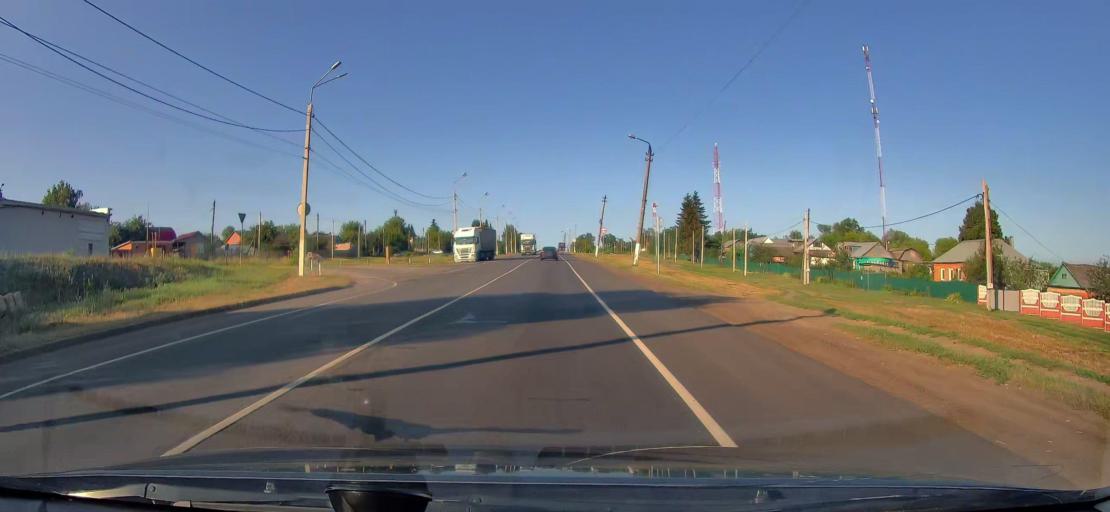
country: RU
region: Tula
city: Plavsk
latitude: 53.6985
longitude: 37.2826
